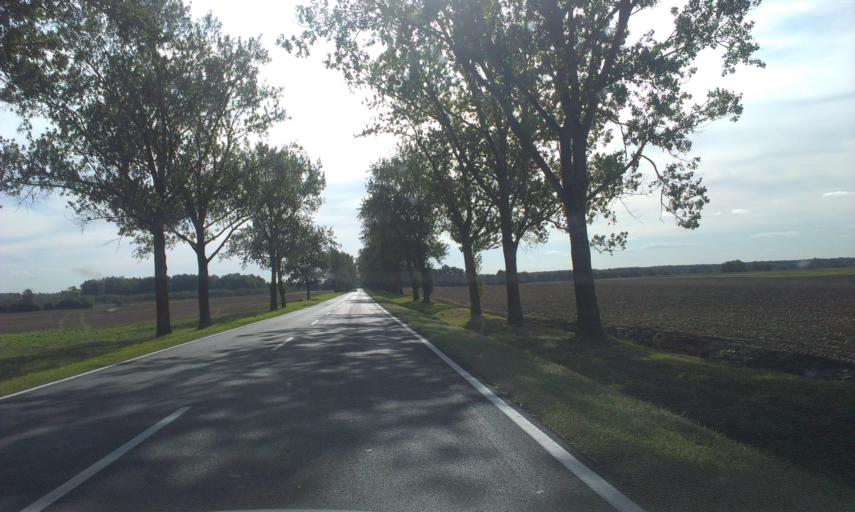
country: PL
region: Greater Poland Voivodeship
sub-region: Powiat zlotowski
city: Okonek
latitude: 53.5810
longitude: 16.8228
